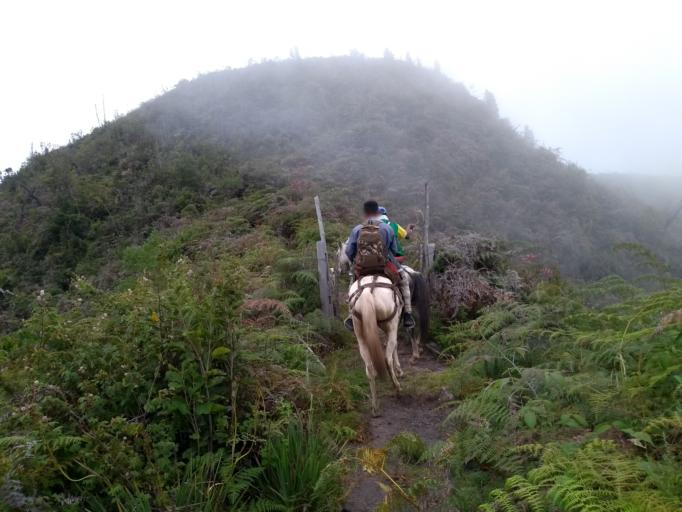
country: CO
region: Cesar
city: Manaure Balcon del Cesar
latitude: 10.1870
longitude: -73.0028
